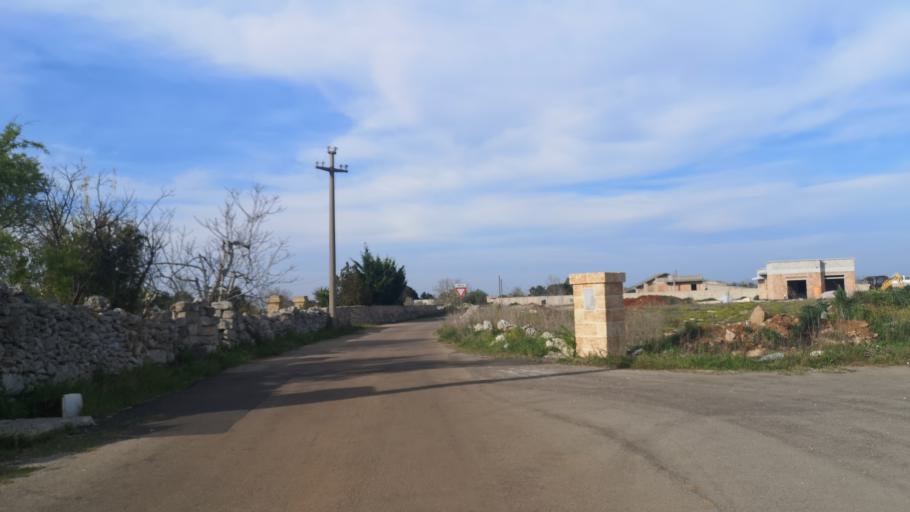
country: IT
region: Apulia
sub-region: Provincia di Lecce
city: Spongano
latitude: 40.0215
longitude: 18.3700
